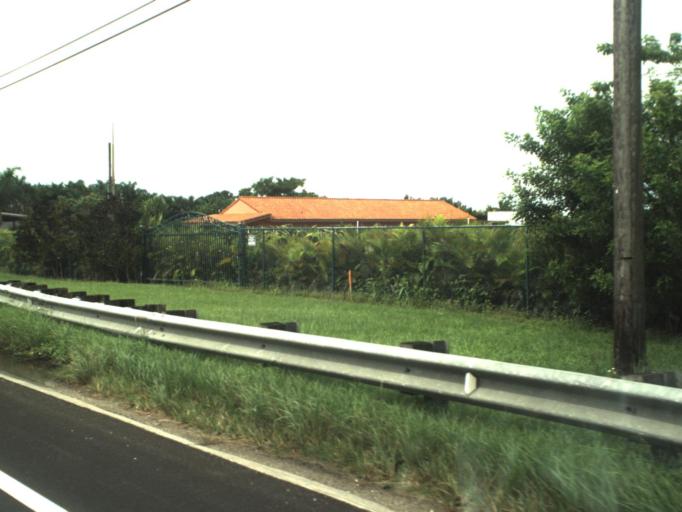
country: US
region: Florida
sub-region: Miami-Dade County
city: Richmond West
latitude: 25.5742
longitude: -80.4783
